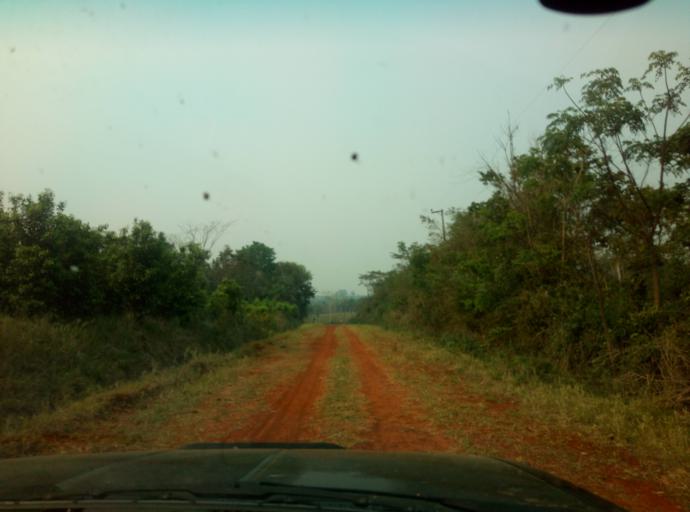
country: PY
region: Caaguazu
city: Carayao
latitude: -25.2085
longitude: -56.2240
